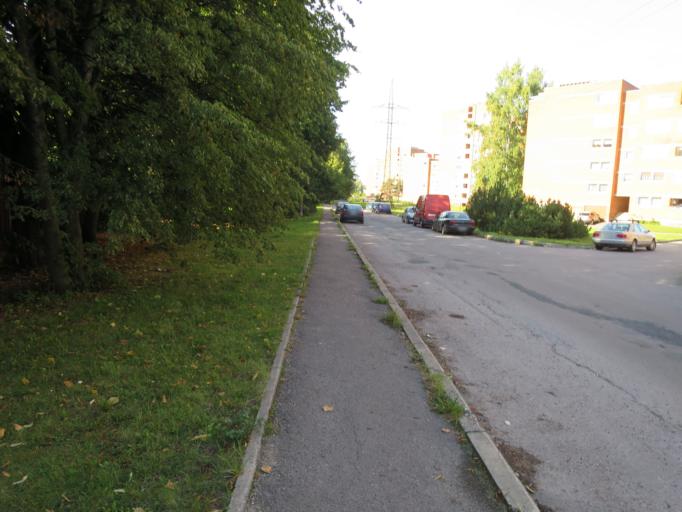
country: EE
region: Harju
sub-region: Tallinna linn
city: Tallinn
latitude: 59.4063
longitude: 24.7075
